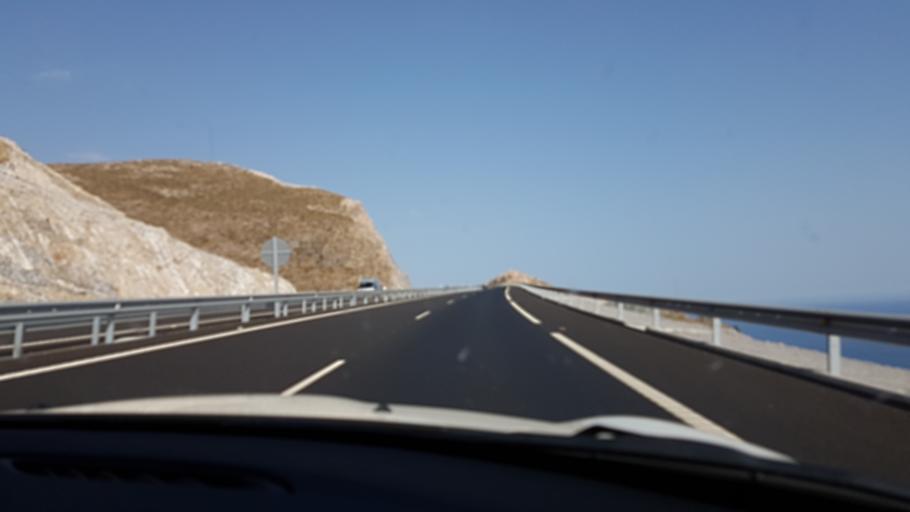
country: ES
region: Andalusia
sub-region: Provincia de Granada
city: Gualchos
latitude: 36.7154
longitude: -3.3918
